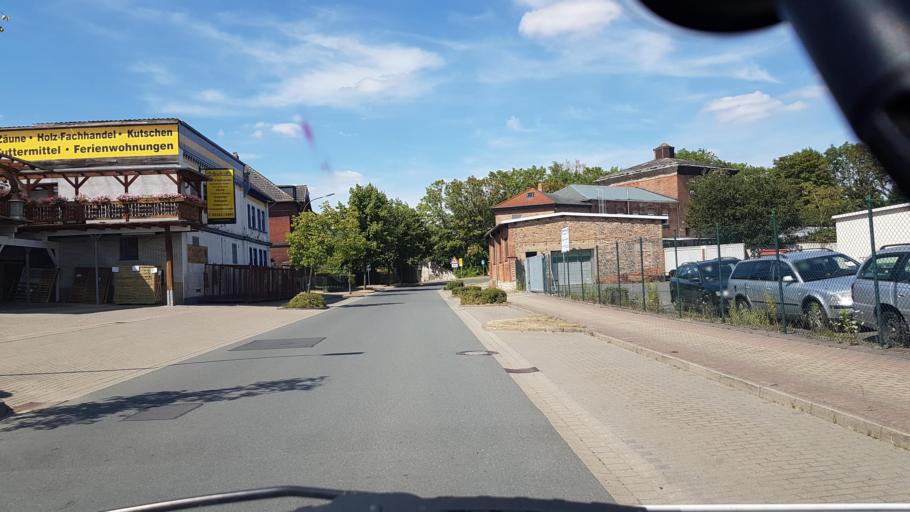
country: DE
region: Lower Saxony
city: Schoningen
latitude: 52.1318
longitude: 10.9734
